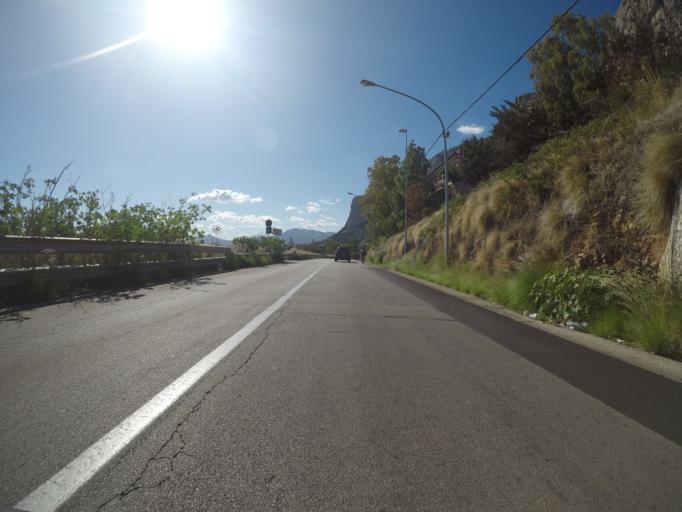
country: IT
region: Sicily
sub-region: Palermo
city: Palermo
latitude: 38.1750
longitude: 13.3661
